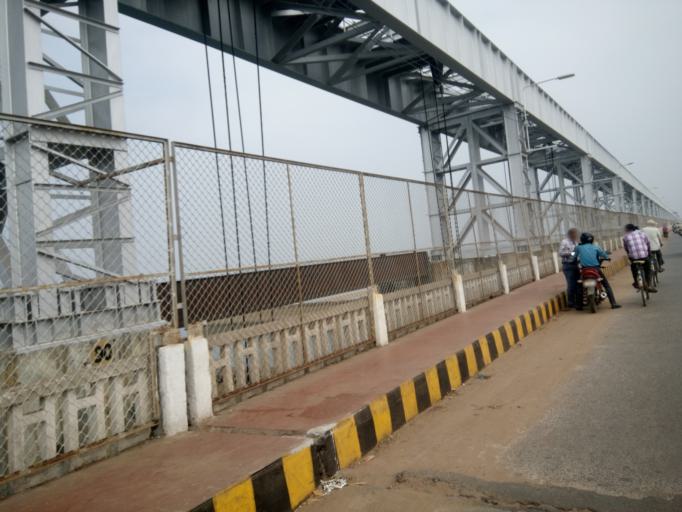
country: IN
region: Odisha
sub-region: Cuttack
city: Cuttack
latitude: 20.4807
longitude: 85.9028
